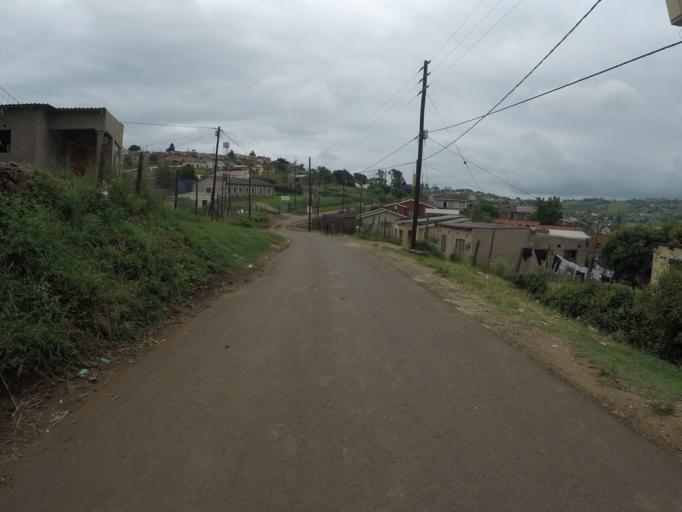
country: ZA
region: KwaZulu-Natal
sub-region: uThungulu District Municipality
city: Empangeni
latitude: -28.7669
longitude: 31.8578
